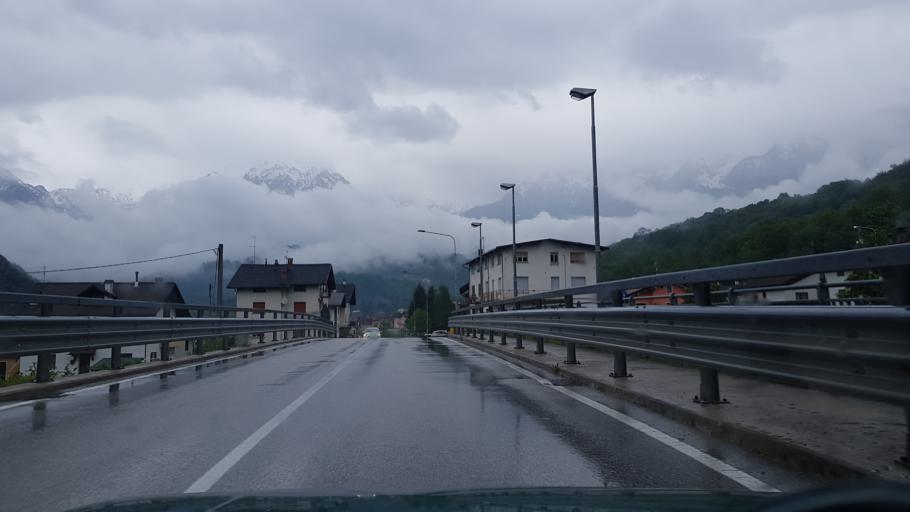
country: IT
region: Veneto
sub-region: Provincia di Belluno
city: Puos d'Alpago
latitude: 46.1391
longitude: 12.3801
